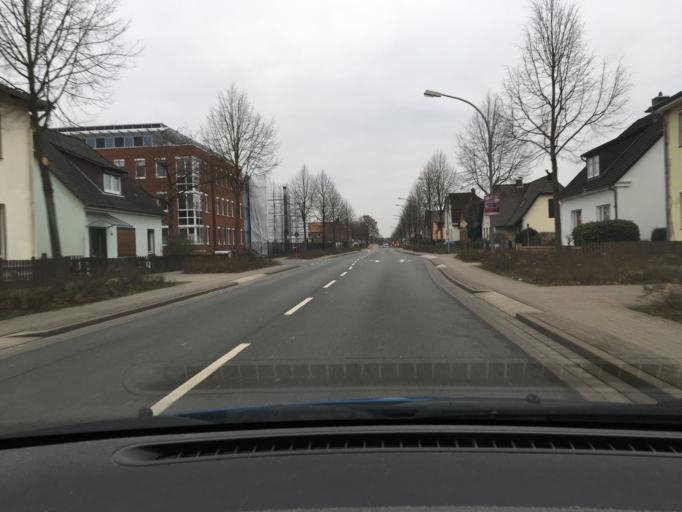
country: DE
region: Lower Saxony
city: Soltau
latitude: 52.9833
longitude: 9.8462
